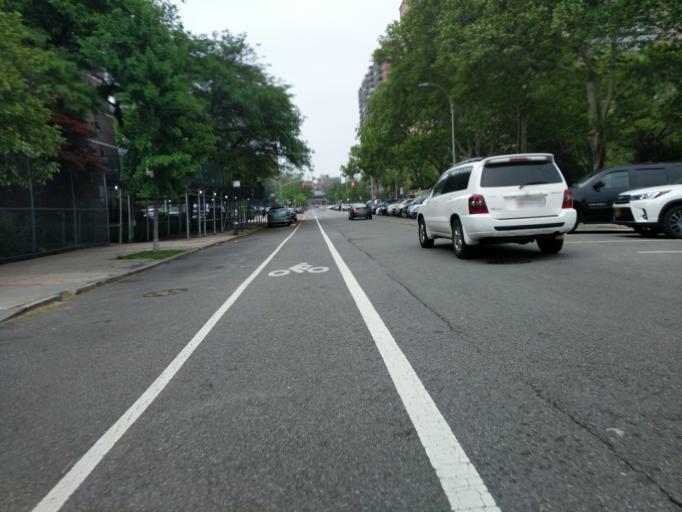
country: US
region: New York
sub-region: Queens County
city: Long Island City
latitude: 40.7064
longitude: -73.9464
